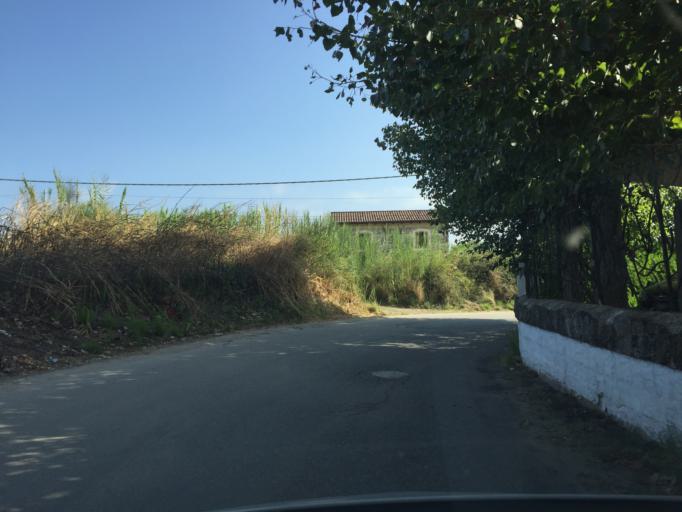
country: IT
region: Calabria
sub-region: Provincia di Vibo-Valentia
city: Briatico
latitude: 38.7207
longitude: 16.0548
